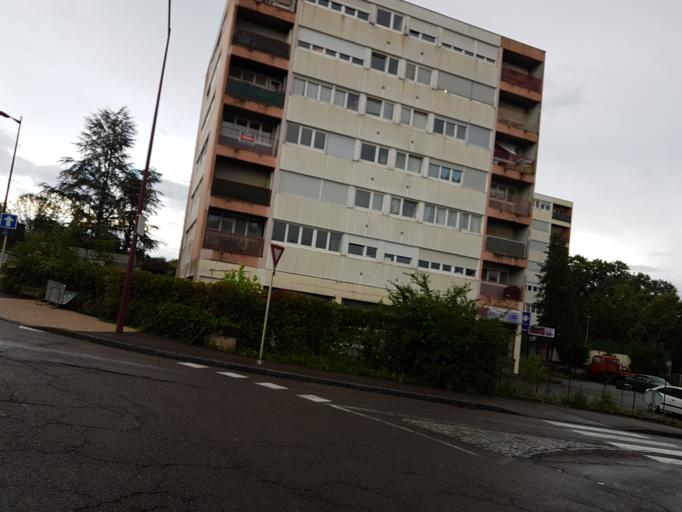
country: FR
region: Franche-Comte
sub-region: Departement de la Haute-Saone
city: Saint-Sauveur
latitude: 47.8098
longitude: 6.3827
